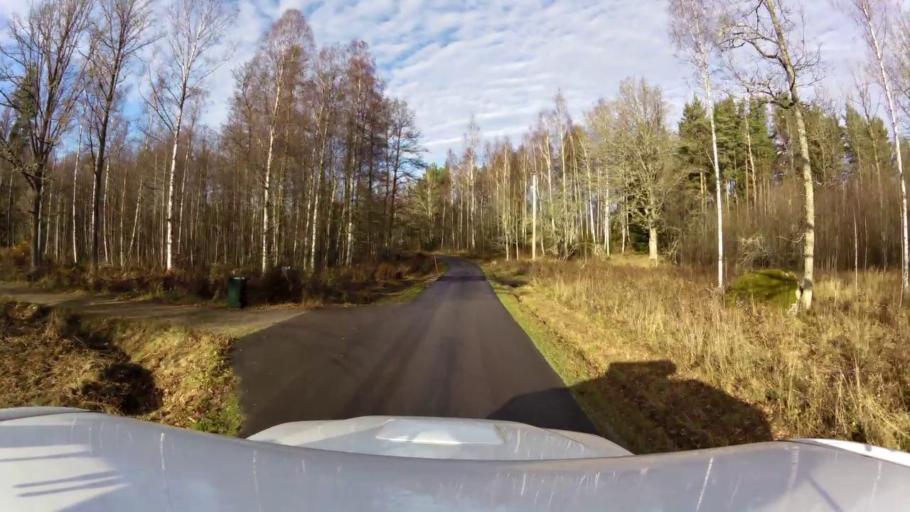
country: SE
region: OEstergoetland
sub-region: Linkopings Kommun
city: Sturefors
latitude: 58.2596
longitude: 15.6923
